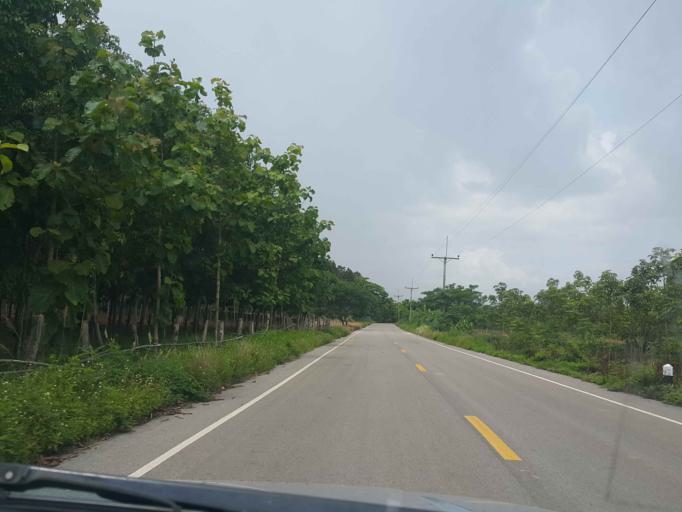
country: TH
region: Phayao
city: Dok Kham Tai
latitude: 19.0465
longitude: 99.9517
